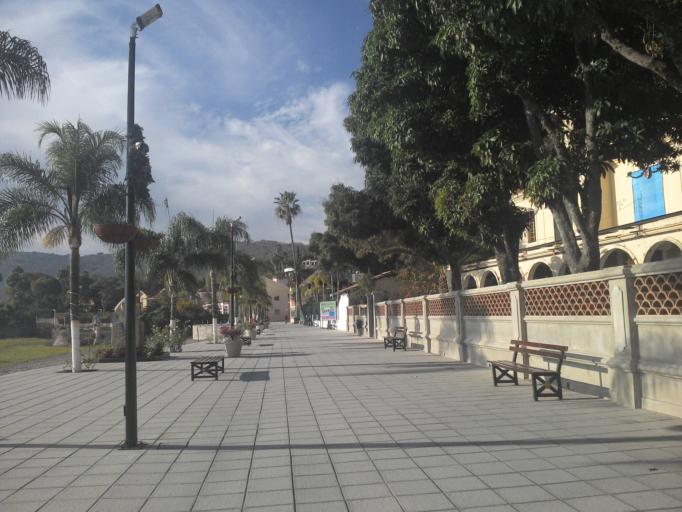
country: MX
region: Jalisco
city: Chapala
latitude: 20.2897
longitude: -103.1946
